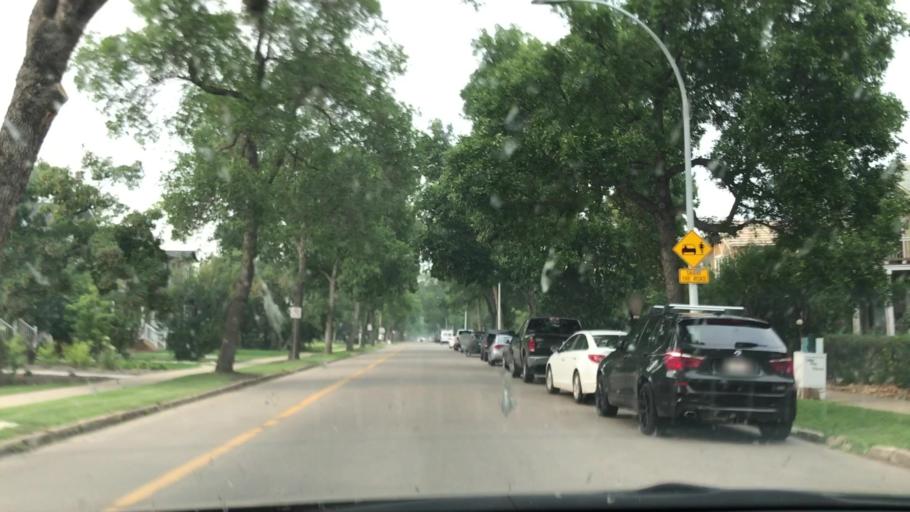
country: CA
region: Alberta
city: Edmonton
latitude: 53.5593
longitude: -113.5412
